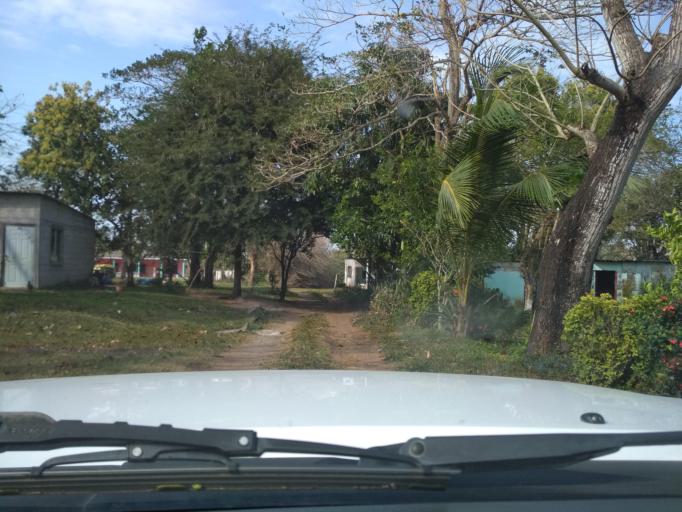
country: MX
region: Veracruz
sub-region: Veracruz
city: Delfino Victoria (Santa Fe)
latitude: 19.1521
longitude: -96.2988
